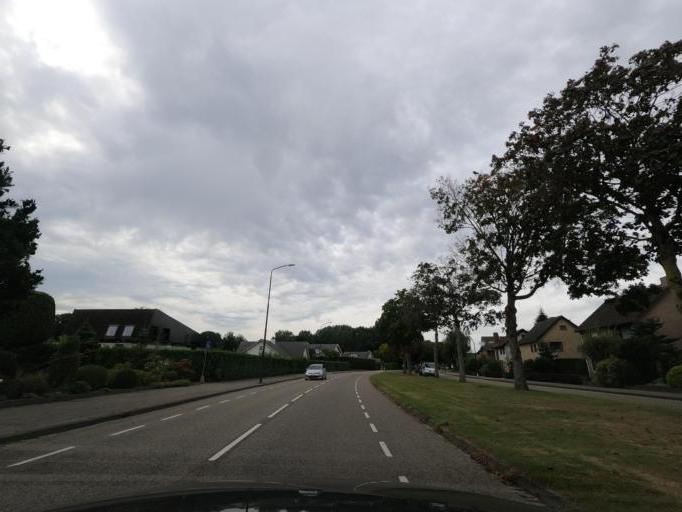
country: NL
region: North Brabant
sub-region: Gemeente Geertruidenberg
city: Geertruidenberg
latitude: 51.6900
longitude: 4.8809
